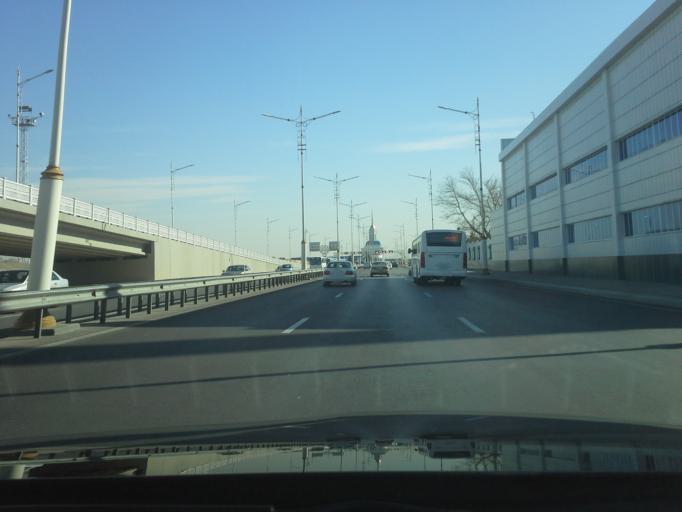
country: TM
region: Ahal
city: Ashgabat
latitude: 37.9464
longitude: 58.3892
